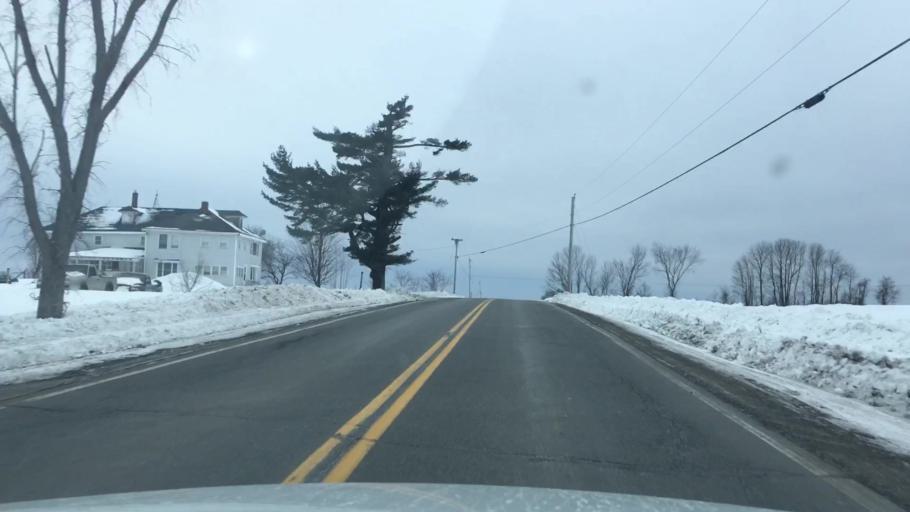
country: US
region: Maine
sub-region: Penobscot County
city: Garland
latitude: 44.9668
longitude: -69.1660
